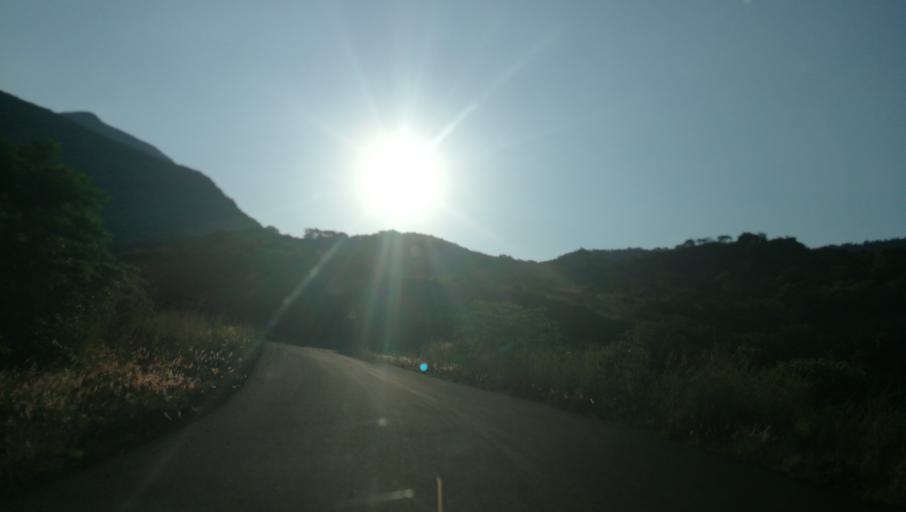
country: ET
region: Southern Nations, Nationalities, and People's Region
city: Areka
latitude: 6.8361
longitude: 37.2808
